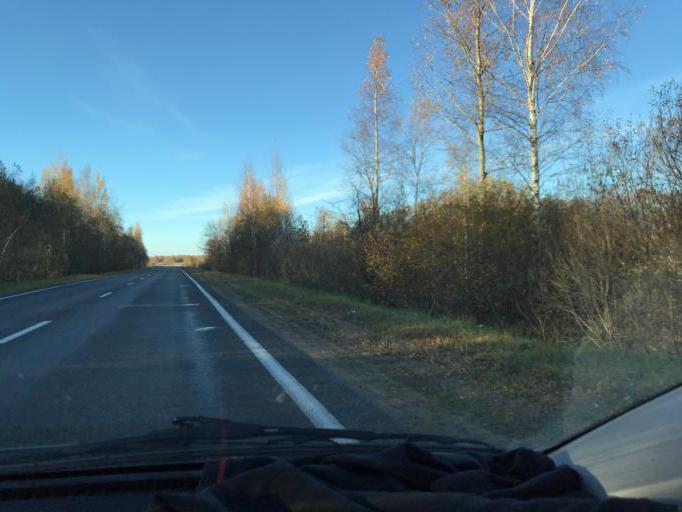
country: BY
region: Vitebsk
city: Haradok
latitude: 55.4196
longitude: 30.1029
